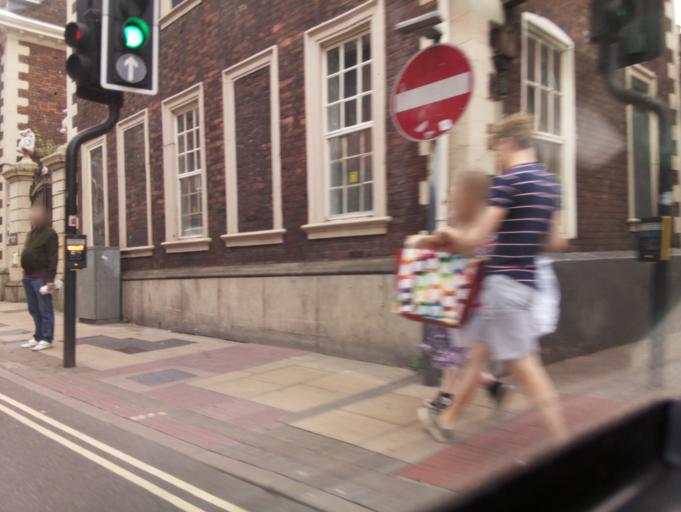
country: GB
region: England
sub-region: Worcestershire
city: Worcester
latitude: 52.1942
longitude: -2.2216
